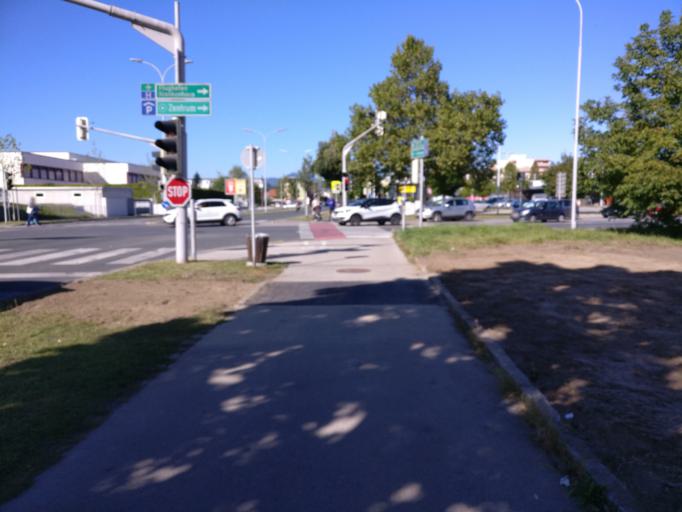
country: AT
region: Carinthia
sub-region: Klagenfurt am Woerthersee
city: Klagenfurt am Woerthersee
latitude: 46.6065
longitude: 14.2908
